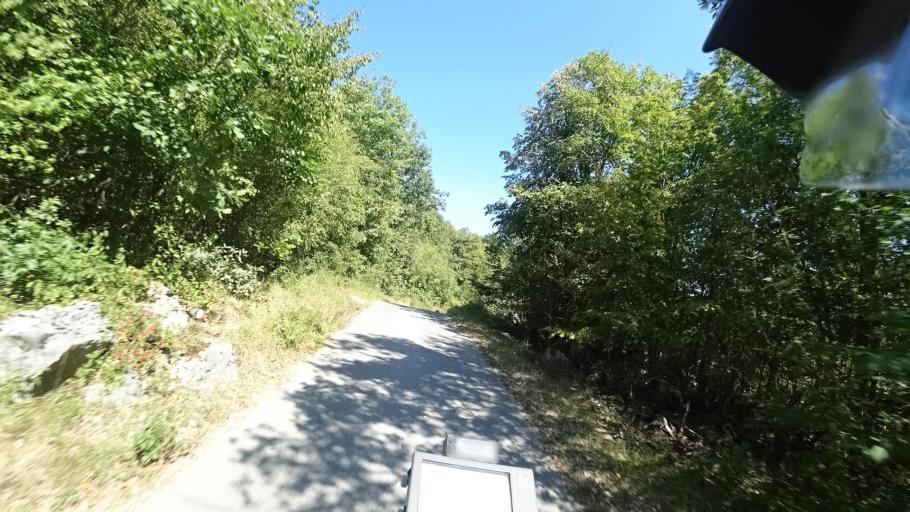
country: HR
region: Licko-Senjska
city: Otocac
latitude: 44.7429
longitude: 15.3724
